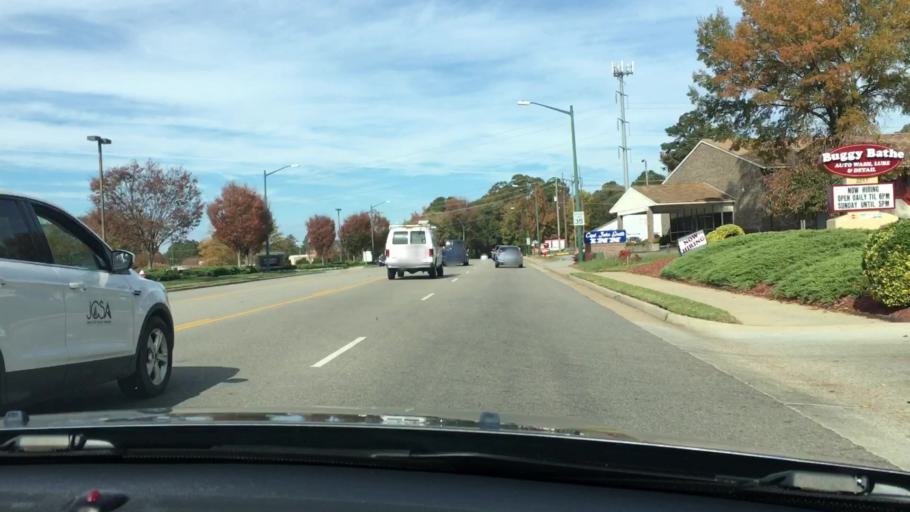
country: US
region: Virginia
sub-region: James City County
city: Williamsburg
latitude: 37.3004
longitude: -76.7275
